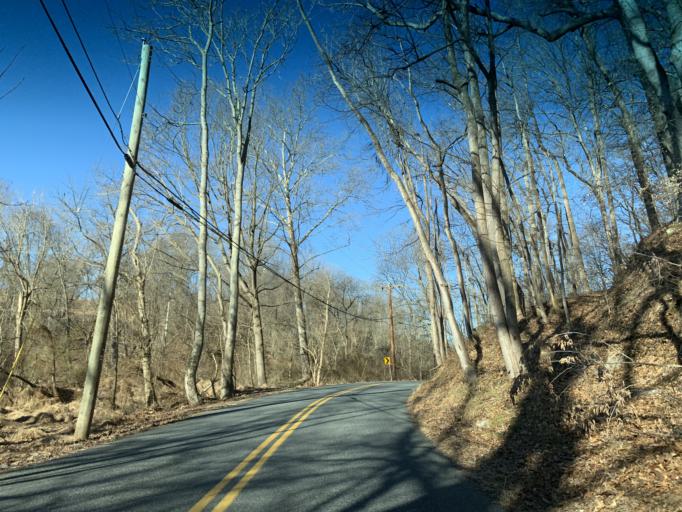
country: US
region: Maryland
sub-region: Harford County
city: South Bel Air
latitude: 39.6292
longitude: -76.2940
